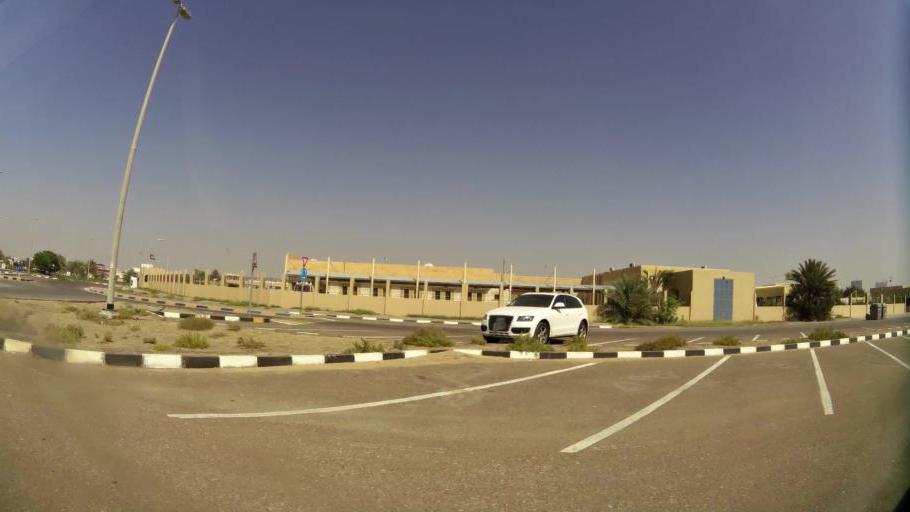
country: AE
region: Ajman
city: Ajman
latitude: 25.4142
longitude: 55.4709
